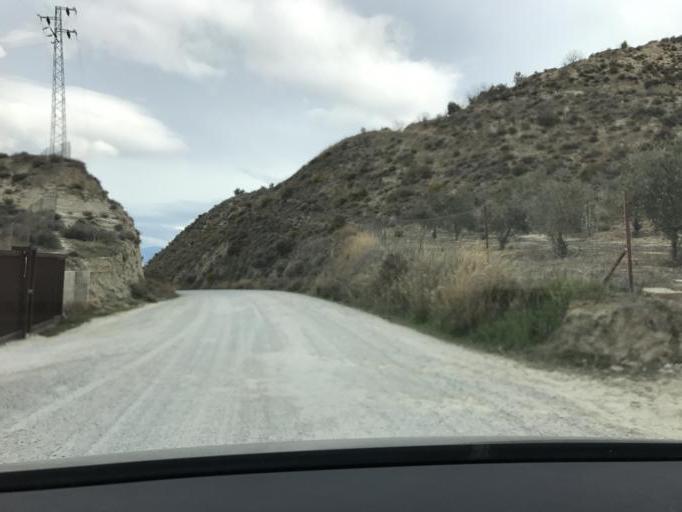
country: ES
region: Andalusia
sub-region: Provincia de Granada
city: Alhendin
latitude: 37.0901
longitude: -3.6633
